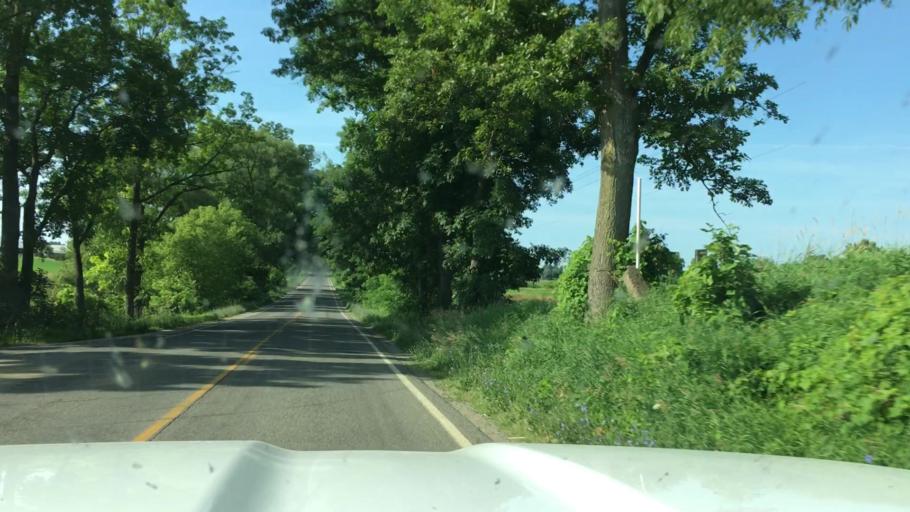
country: US
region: Michigan
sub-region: Barry County
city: Stony Point
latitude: 42.4316
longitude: -85.4545
